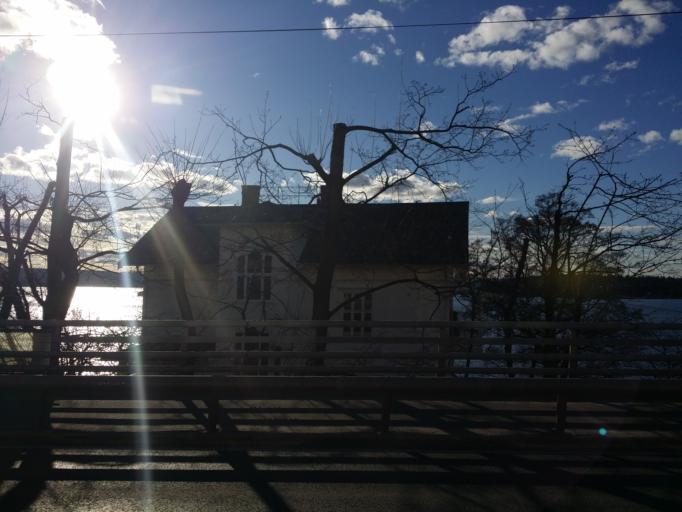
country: NO
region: Akershus
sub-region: Oppegard
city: Kolbotn
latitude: 59.8565
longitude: 10.7847
